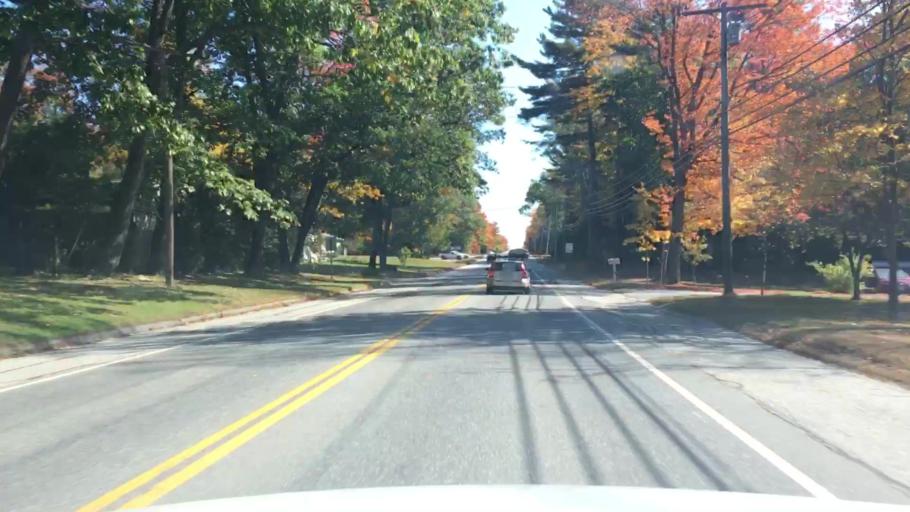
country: US
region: Maine
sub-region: Sagadahoc County
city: Topsham
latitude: 43.9496
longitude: -69.9914
